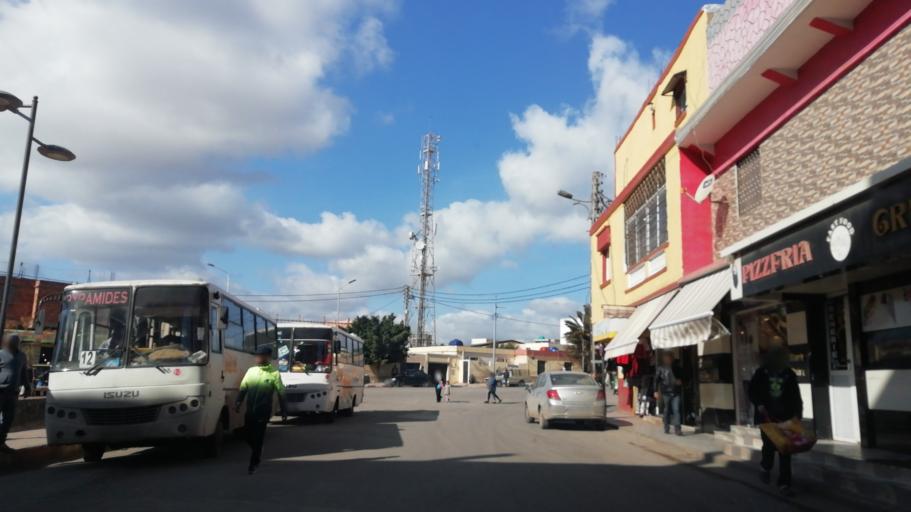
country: DZ
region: Oran
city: Es Senia
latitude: 35.6393
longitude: -0.6669
